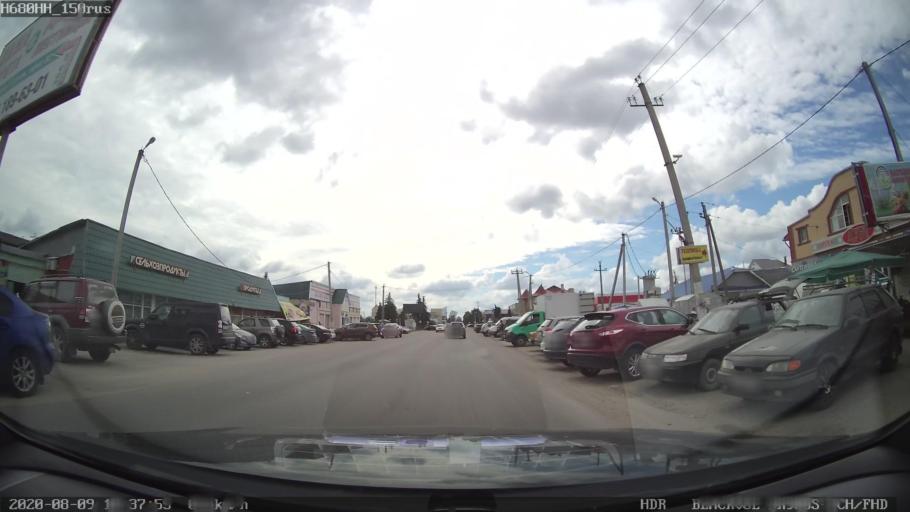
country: RU
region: Tula
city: Zaokskiy
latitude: 54.7360
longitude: 37.3981
